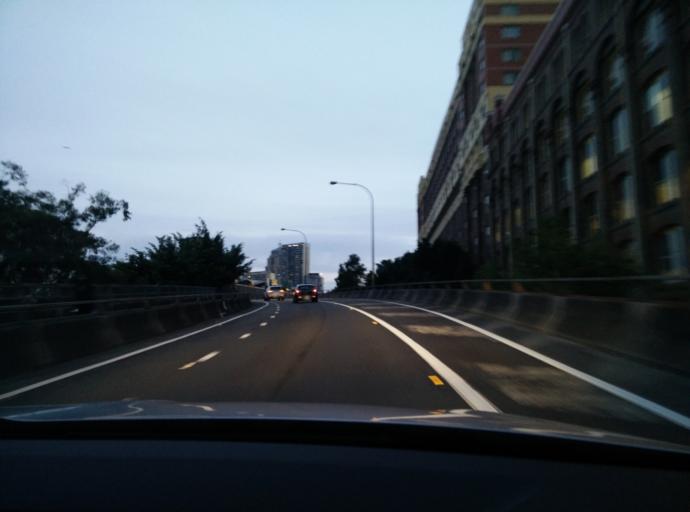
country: AU
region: New South Wales
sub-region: City of Sydney
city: Haymarket
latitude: -33.8729
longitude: 151.1970
